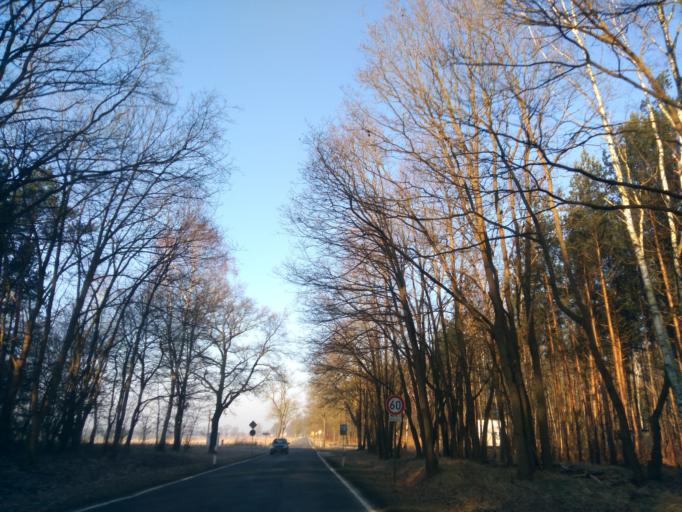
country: DE
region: Brandenburg
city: Falkensee
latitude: 52.6308
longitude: 13.0766
